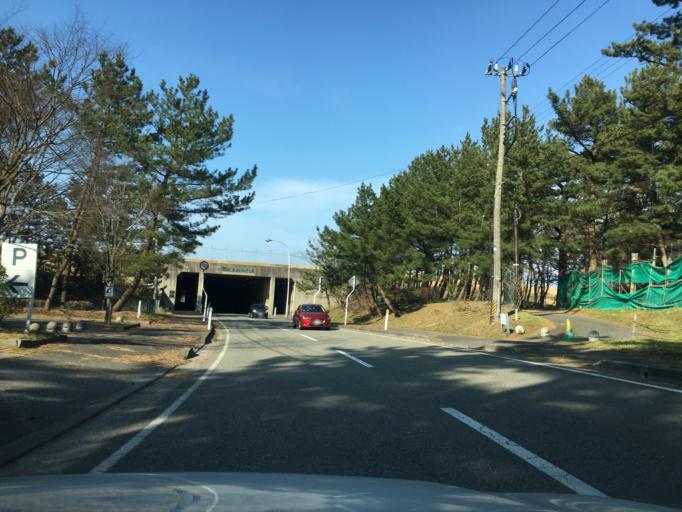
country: JP
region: Yamagata
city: Tsuruoka
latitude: 38.8088
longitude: 139.7786
